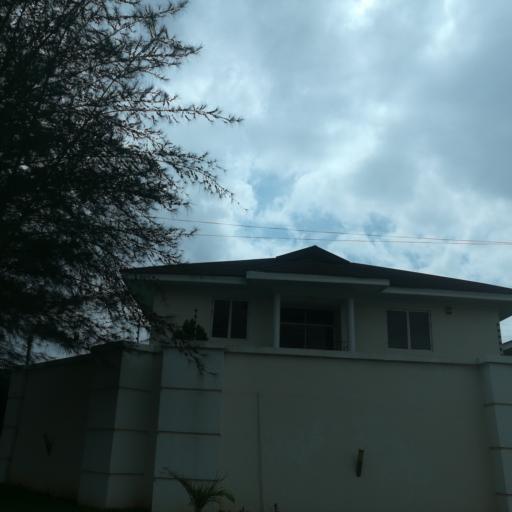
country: NG
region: Lagos
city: Ikoyi
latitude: 6.4379
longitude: 3.4584
